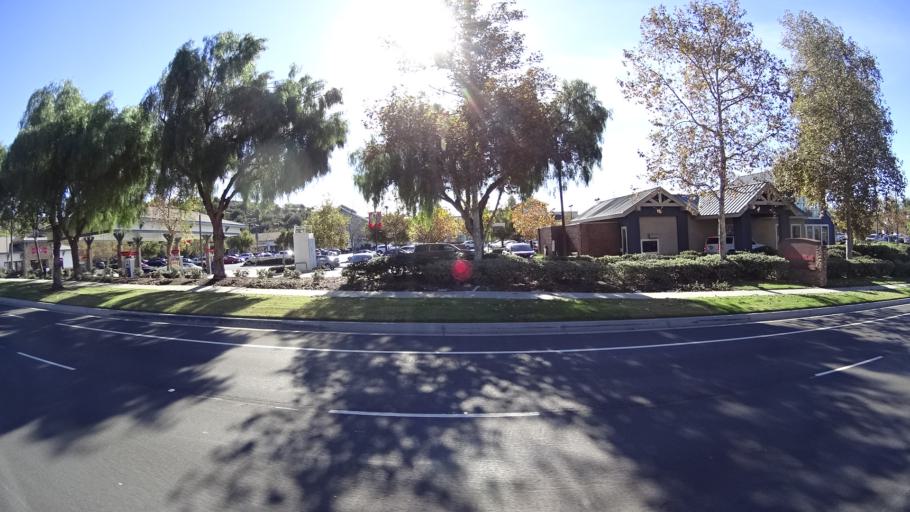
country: US
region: California
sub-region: Orange County
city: Ladera Ranch
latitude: 33.5636
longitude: -117.6470
